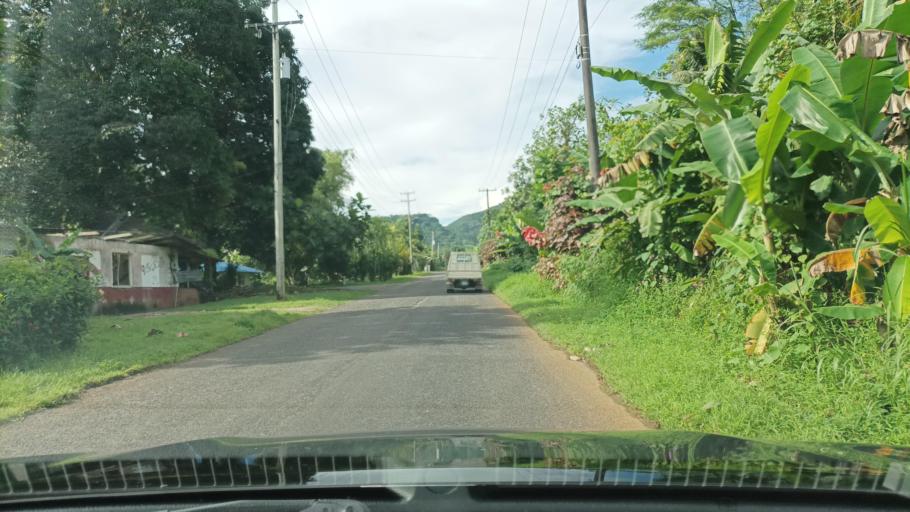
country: FM
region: Pohnpei
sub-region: Kolonia Municipality
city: Kolonia Town
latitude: 6.9463
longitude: 158.1951
